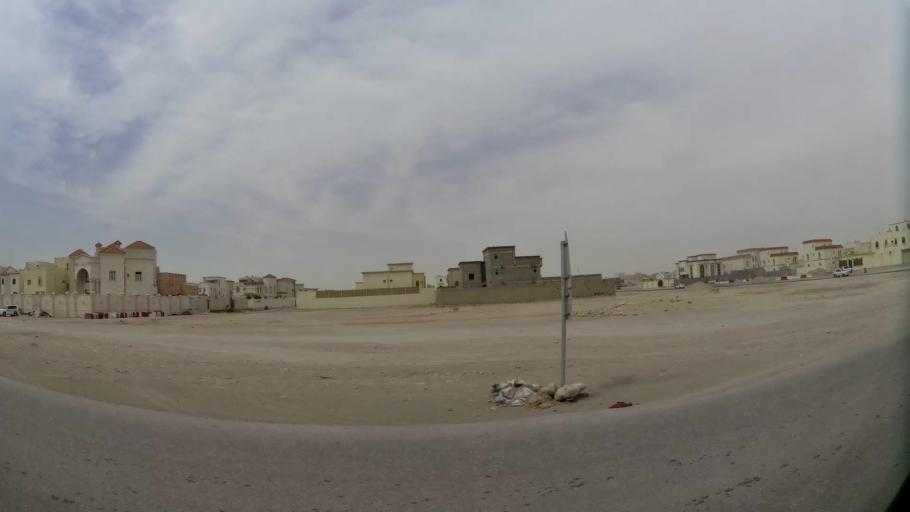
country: QA
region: Baladiyat ar Rayyan
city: Ar Rayyan
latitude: 25.2087
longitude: 51.4567
